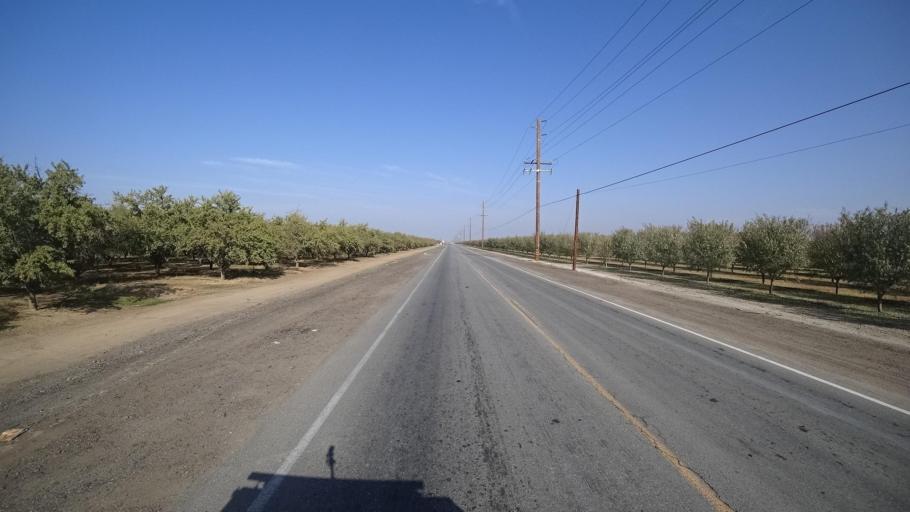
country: US
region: California
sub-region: Kern County
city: McFarland
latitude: 35.7184
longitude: -119.2231
